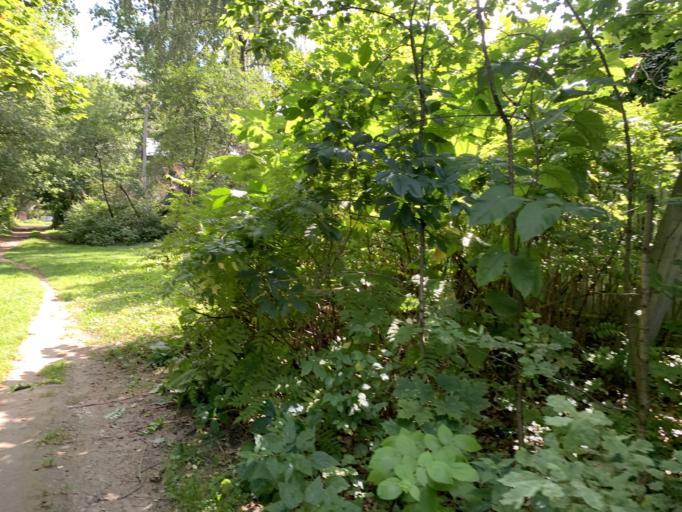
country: RU
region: Moskovskaya
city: Mamontovka
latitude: 55.9667
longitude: 37.8273
